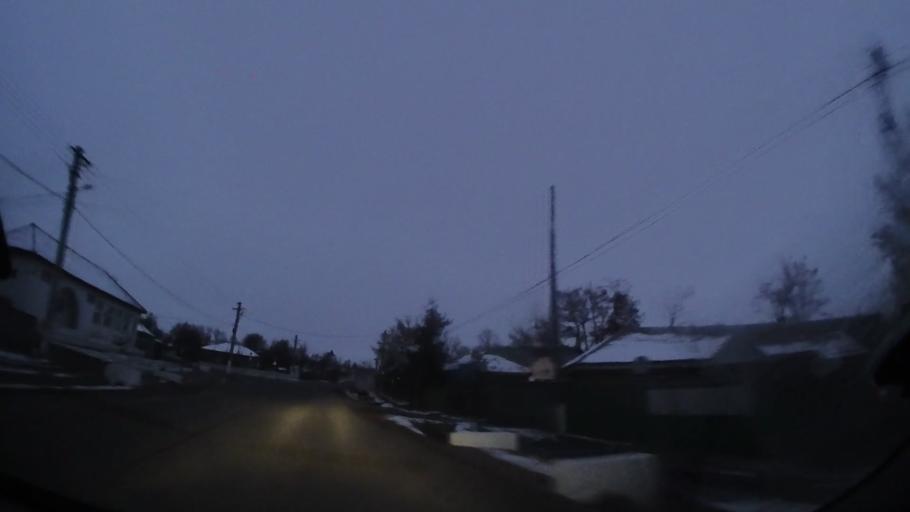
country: RO
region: Vaslui
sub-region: Comuna Dimitrie Cantemir
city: Dimitrie Cantemir
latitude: 46.5062
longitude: 28.0554
